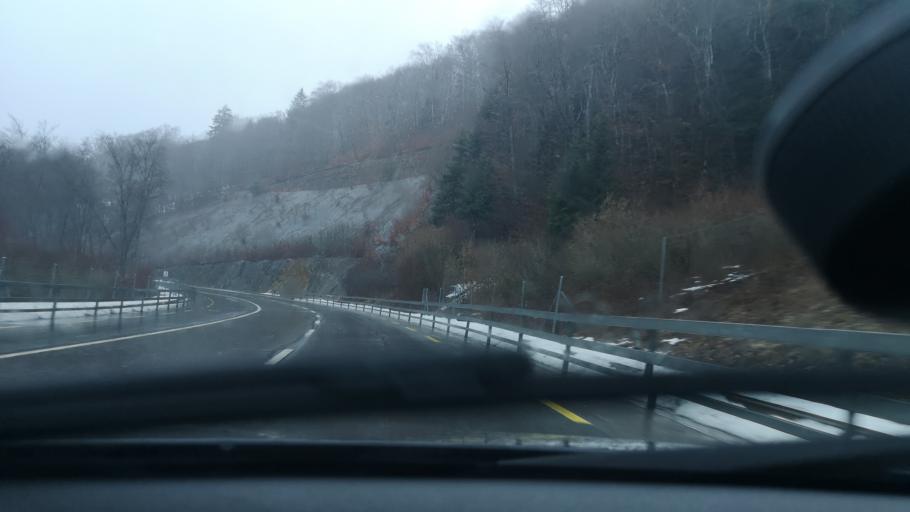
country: CH
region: Neuchatel
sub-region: Boudry District
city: Bevaix
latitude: 46.9684
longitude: 6.7844
